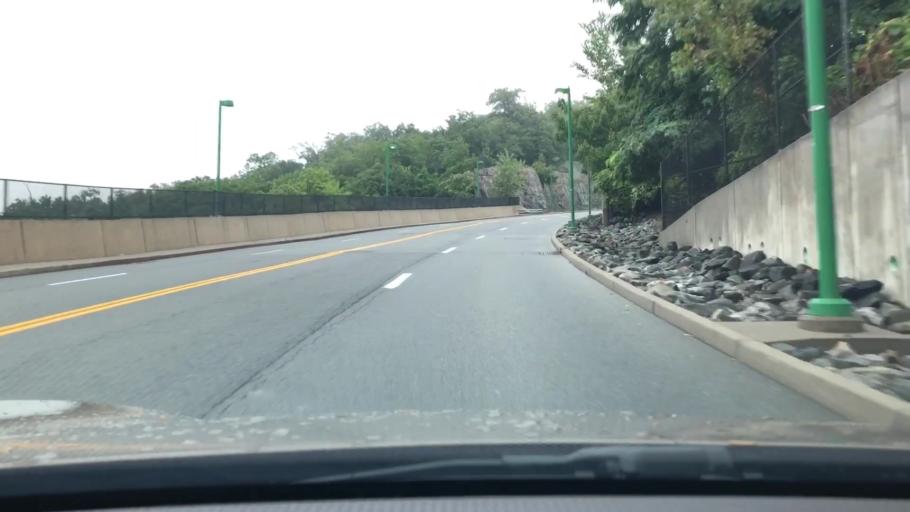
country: US
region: New York
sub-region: Westchester County
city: Tuckahoe
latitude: 40.9564
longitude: -73.8576
